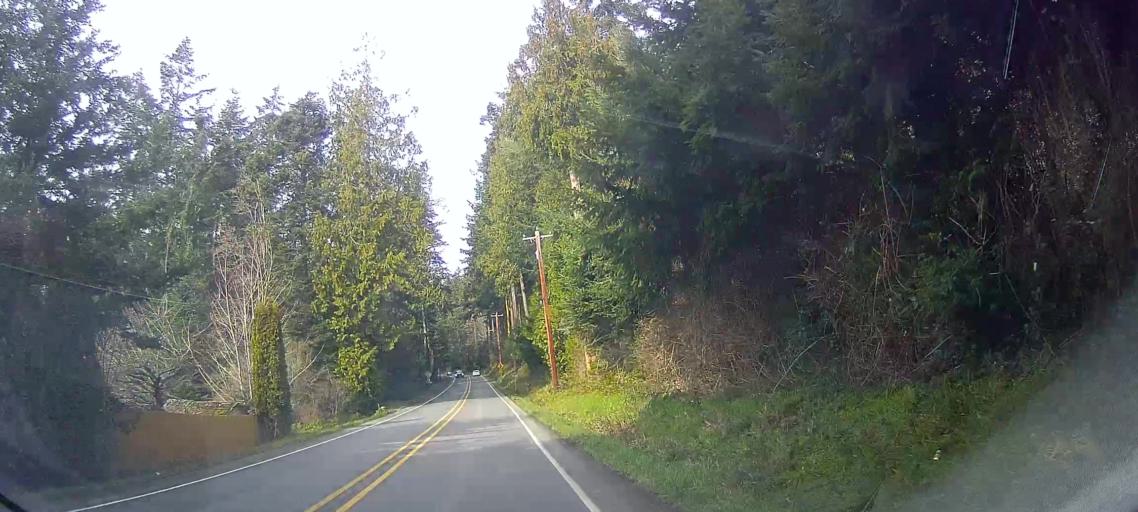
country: US
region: Washington
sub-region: Island County
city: Langley
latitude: 48.1105
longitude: -122.4450
